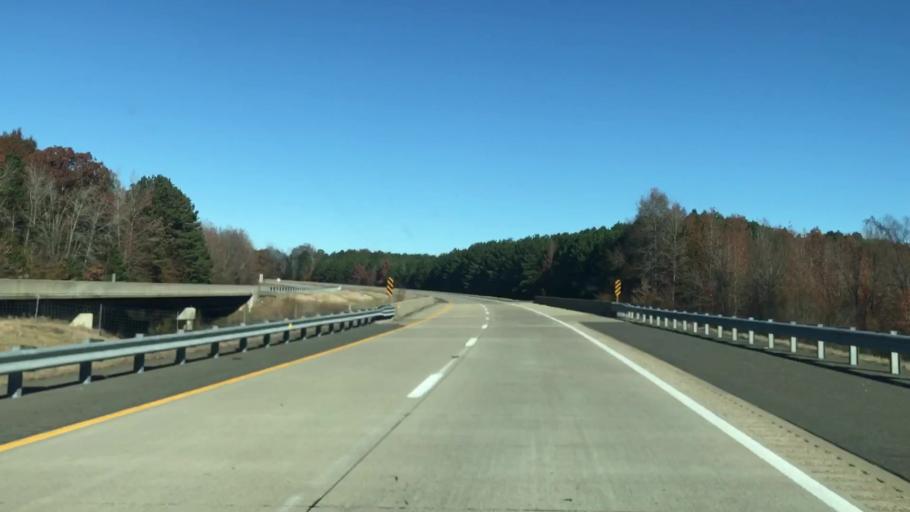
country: US
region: Texas
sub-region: Bowie County
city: Texarkana
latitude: 33.2401
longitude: -93.8732
